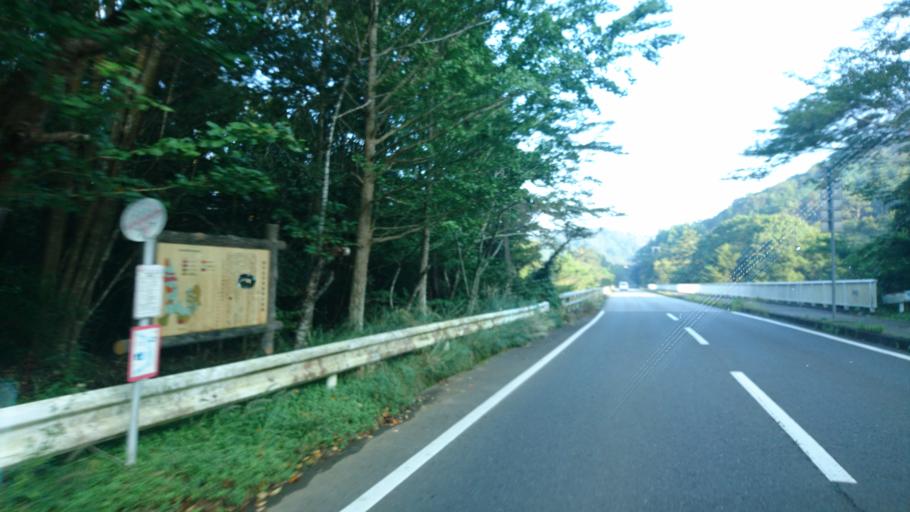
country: JP
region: Chiba
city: Kawaguchi
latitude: 35.1747
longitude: 140.0090
